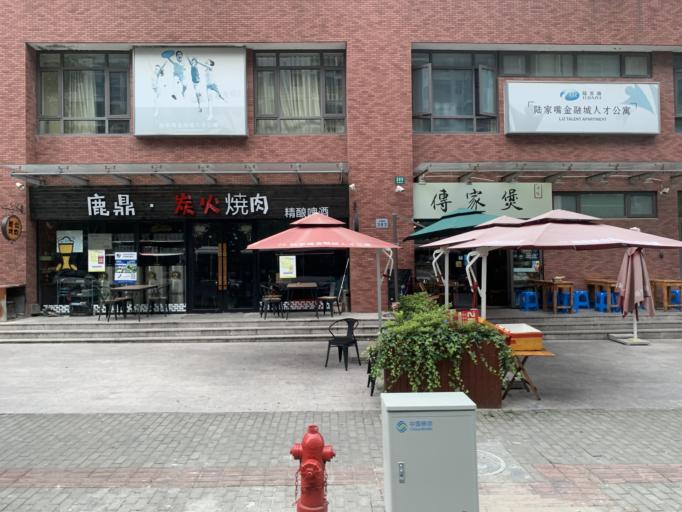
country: CN
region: Shanghai Shi
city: Huamu
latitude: 31.2025
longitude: 121.5305
